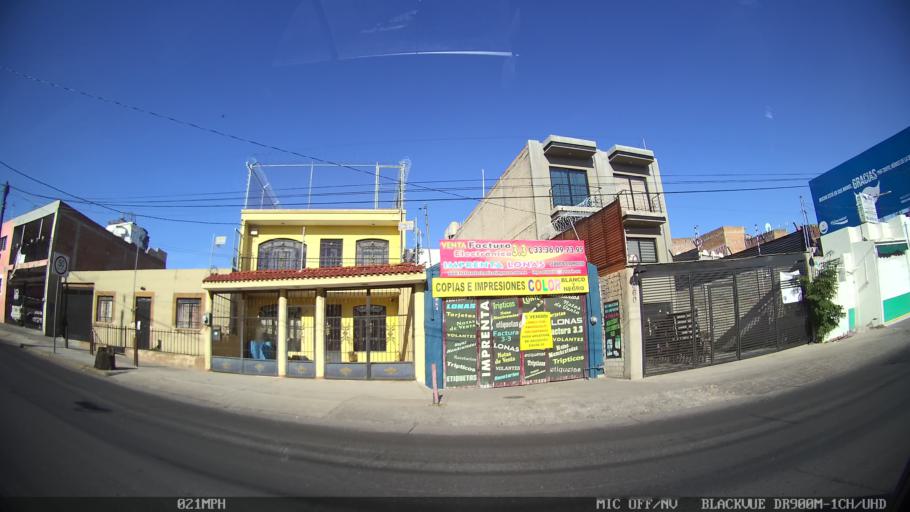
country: MX
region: Jalisco
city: Tlaquepaque
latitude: 20.6888
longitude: -103.3249
